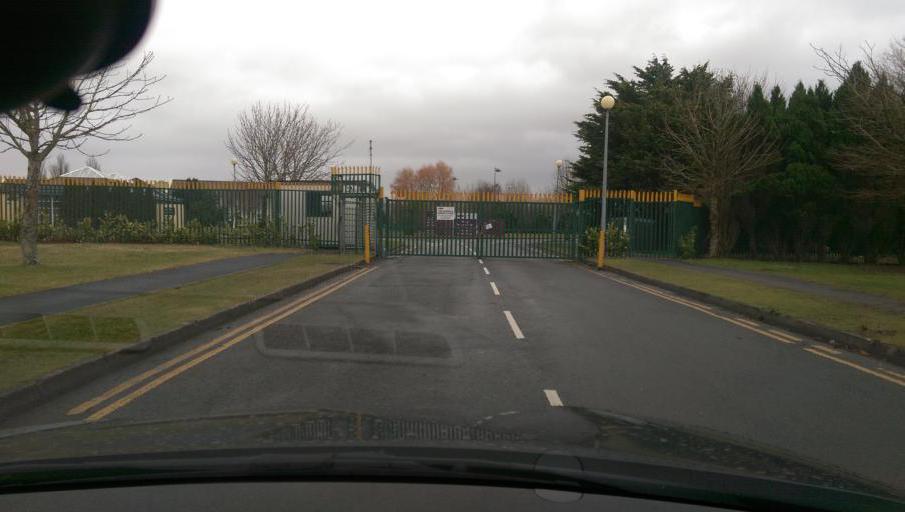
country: IE
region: Connaught
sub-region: County Galway
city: Gaillimh
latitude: 53.2880
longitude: -9.0671
